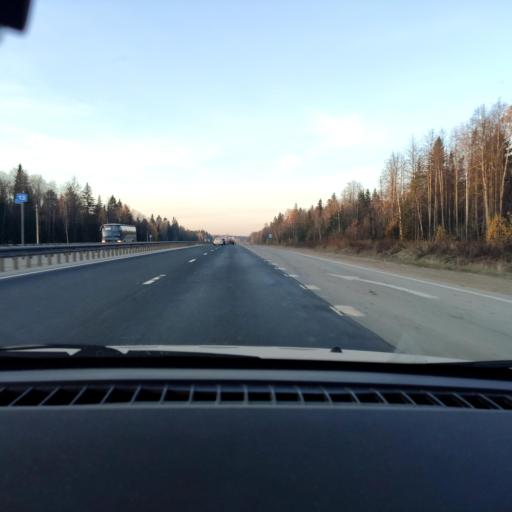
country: RU
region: Perm
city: Ferma
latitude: 58.0257
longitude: 56.4267
